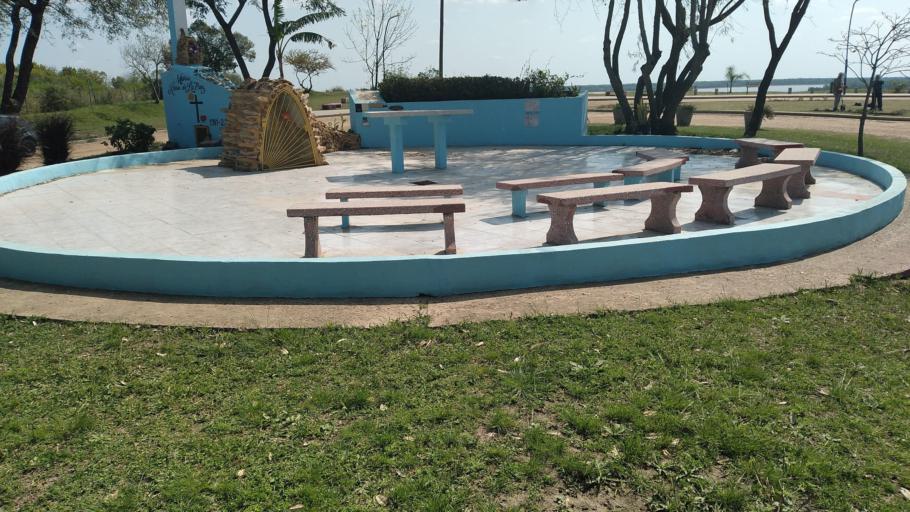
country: AR
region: Entre Rios
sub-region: Departamento de La Paz
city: La Paz
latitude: -30.7509
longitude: -59.6548
